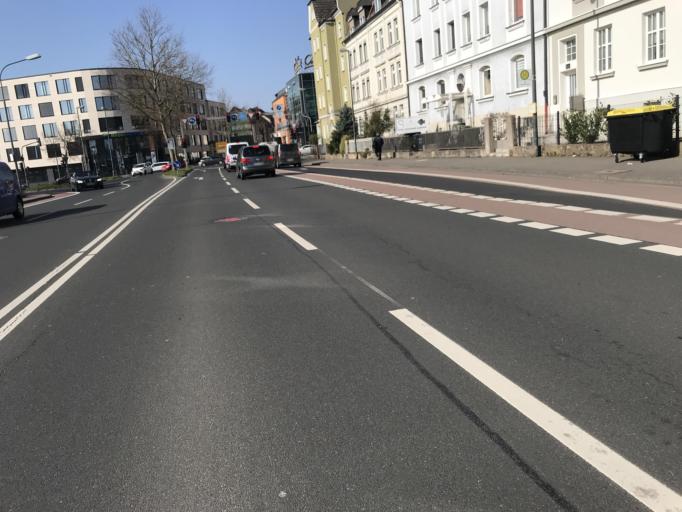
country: DE
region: Hesse
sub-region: Regierungsbezirk Kassel
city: Fulda
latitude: 50.5457
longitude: 9.6751
